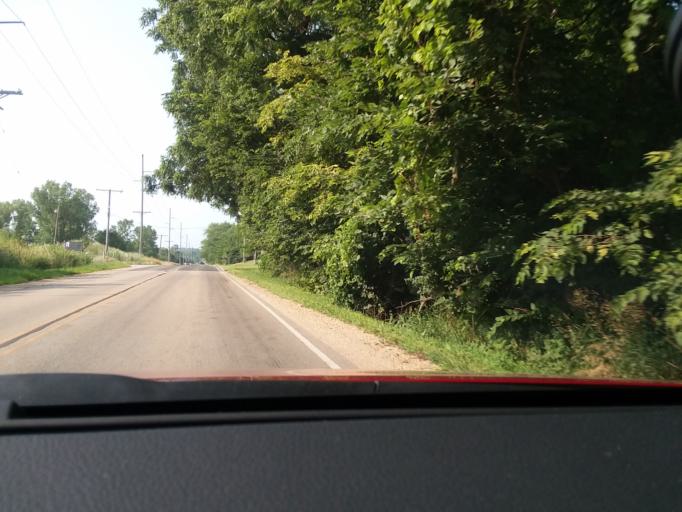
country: US
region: Wisconsin
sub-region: Dane County
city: Sun Prairie
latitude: 43.1283
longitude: -89.2664
